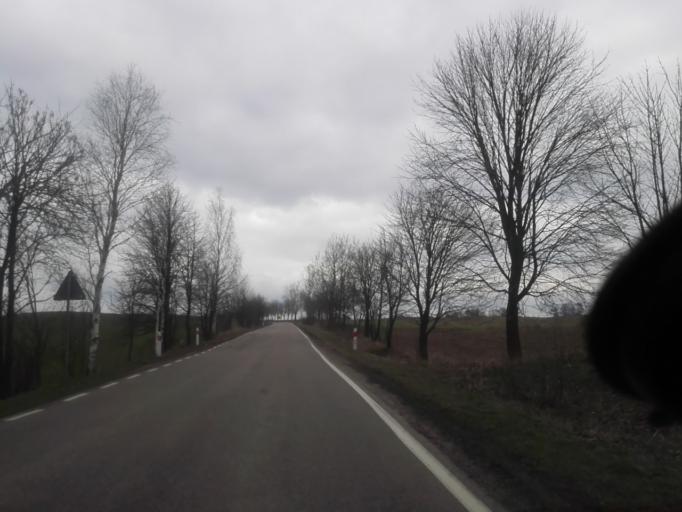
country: PL
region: Podlasie
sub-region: Suwalki
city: Suwalki
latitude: 54.2357
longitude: 22.9143
